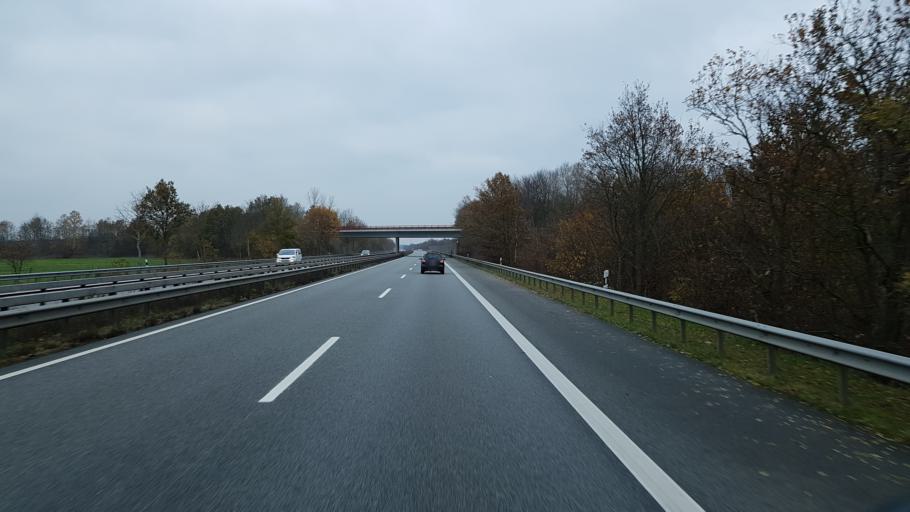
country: DE
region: Lower Saxony
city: Driftsethe
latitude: 53.4075
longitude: 8.5803
